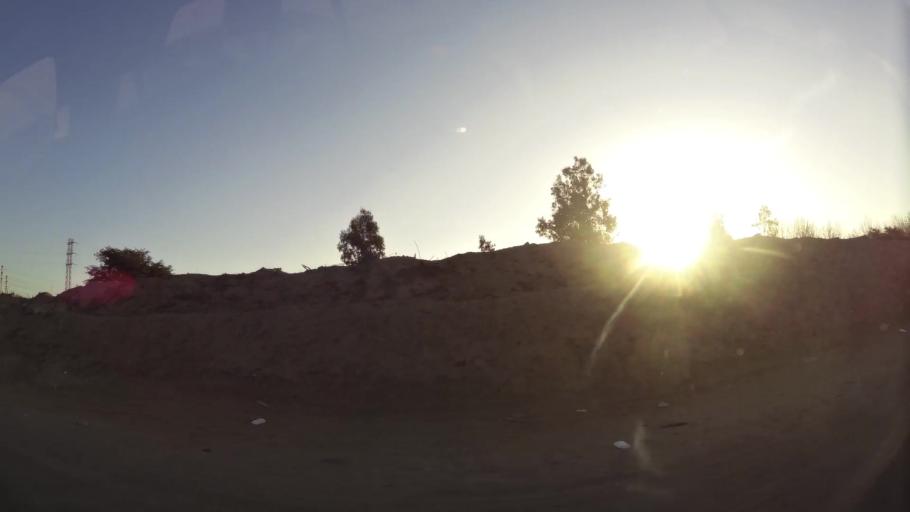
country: PE
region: Ica
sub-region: Provincia de Ica
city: Ica
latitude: -14.0892
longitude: -75.7181
